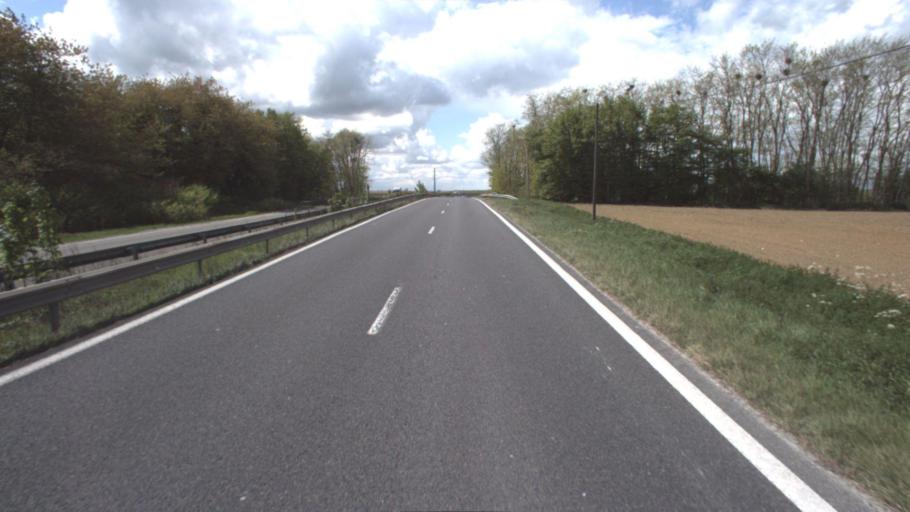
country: FR
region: Ile-de-France
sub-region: Departement de Seine-et-Marne
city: Jouy-le-Chatel
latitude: 48.6846
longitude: 3.0756
